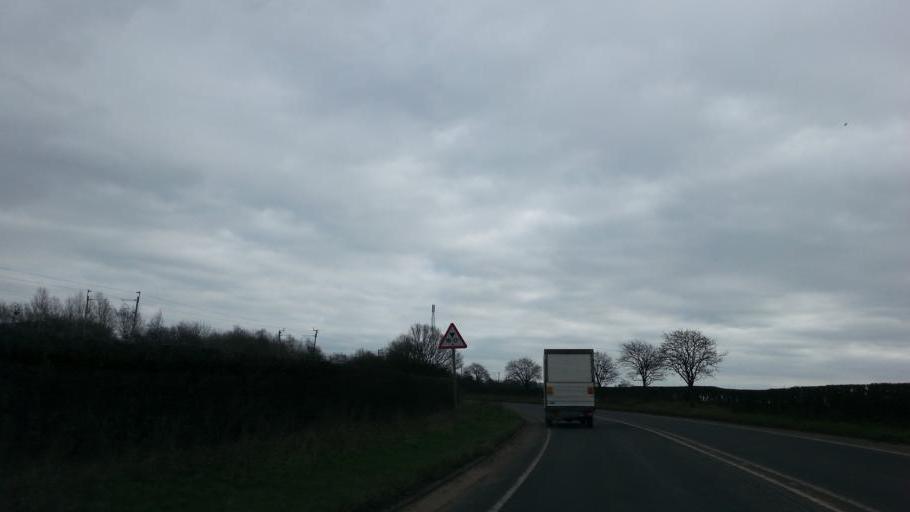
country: GB
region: England
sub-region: Staffordshire
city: Stone
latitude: 52.8807
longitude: -2.1143
